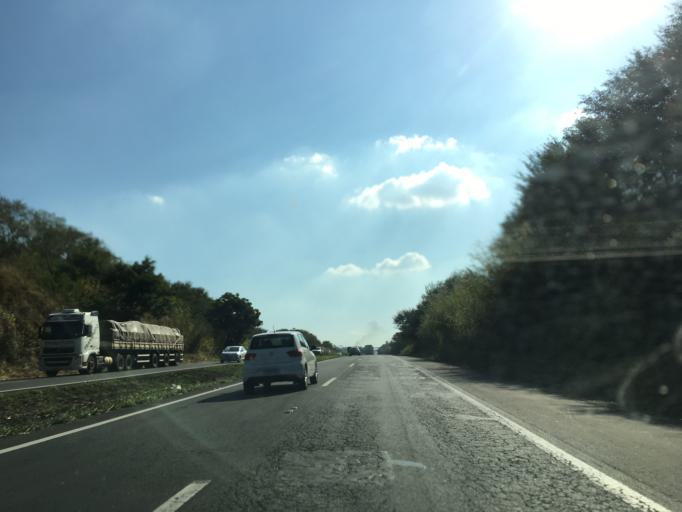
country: BR
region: Sao Paulo
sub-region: Santa Barbara D'Oeste
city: Santa Barbara d'Oeste
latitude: -22.7541
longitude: -47.4837
